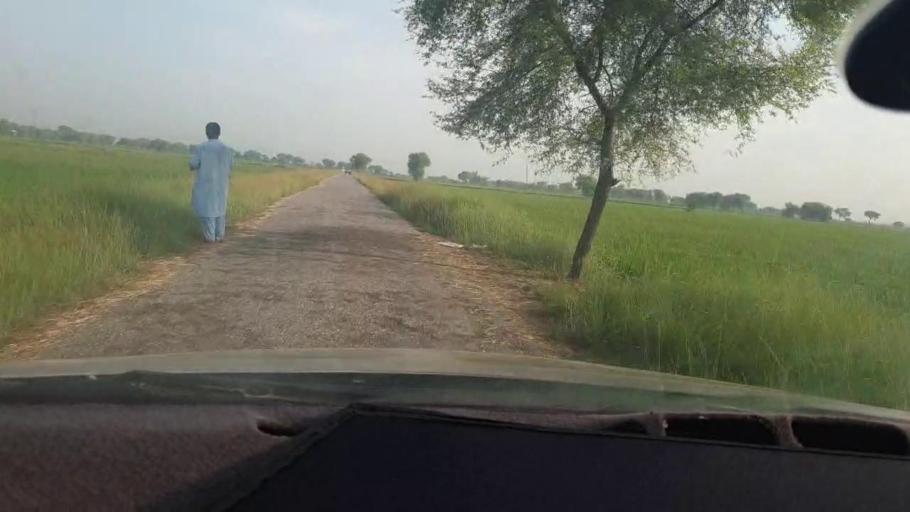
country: PK
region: Sindh
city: Jacobabad
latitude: 28.3038
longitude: 68.4148
